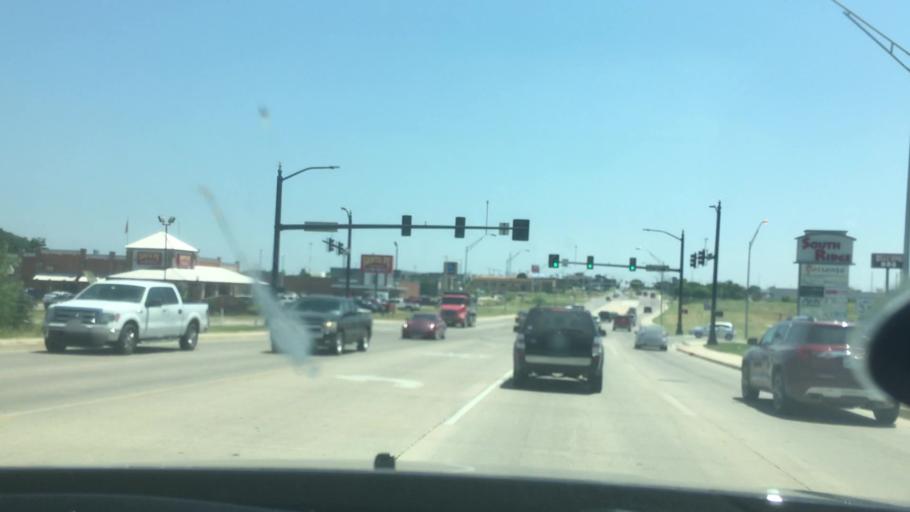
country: US
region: Oklahoma
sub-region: Pontotoc County
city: Ada
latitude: 34.7906
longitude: -96.6611
